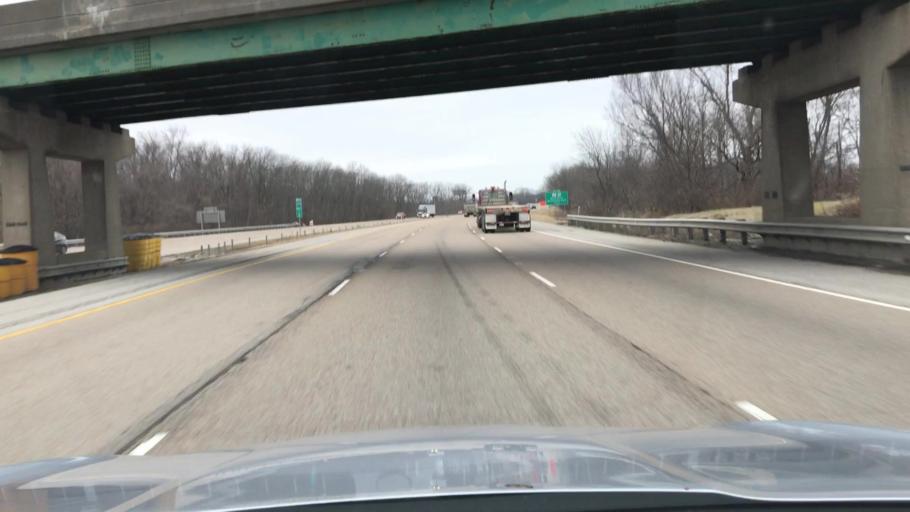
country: US
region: Illinois
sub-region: Saint Clair County
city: Fairmont City
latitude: 38.6630
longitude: -90.0661
